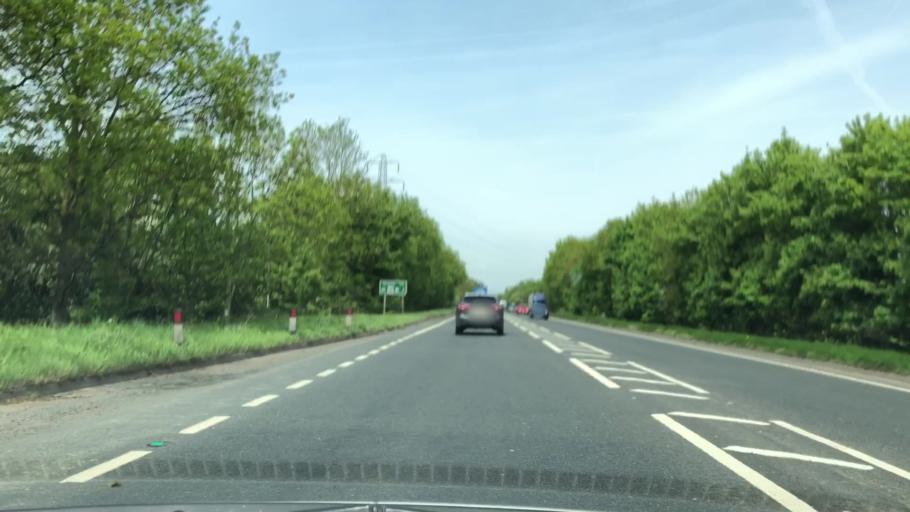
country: GB
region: England
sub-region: Shropshire
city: Gobowen
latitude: 52.9065
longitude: -3.0429
